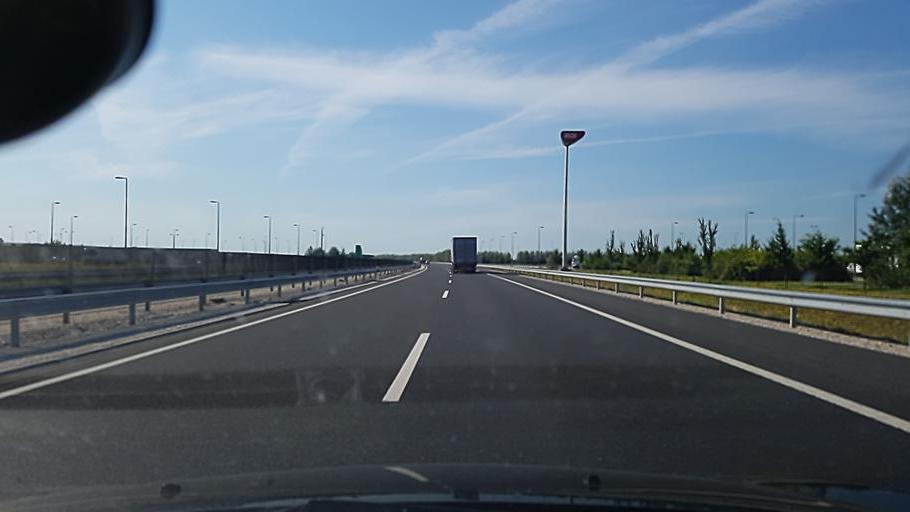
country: HU
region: Tolna
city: Szedres
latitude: 46.4410
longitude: 18.7084
